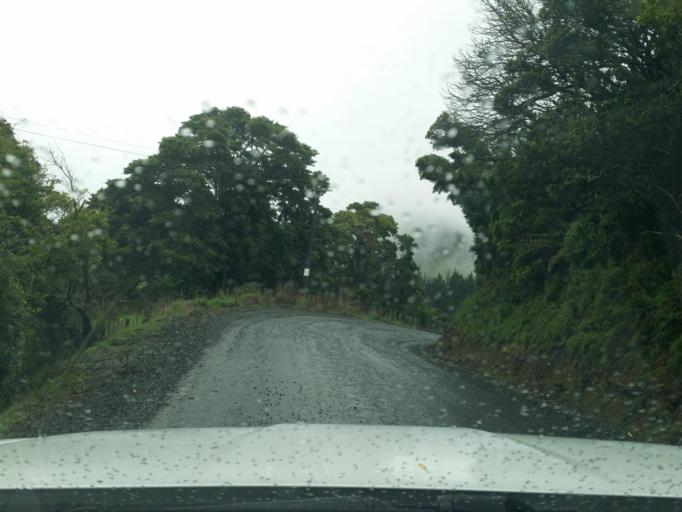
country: NZ
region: Northland
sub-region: Kaipara District
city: Dargaville
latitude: -35.7856
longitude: 173.9883
